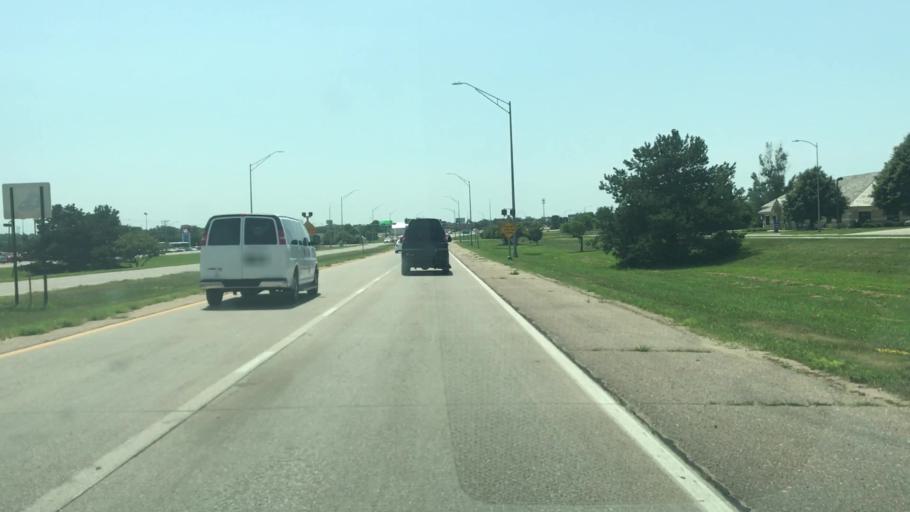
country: US
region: Nebraska
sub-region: Adams County
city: Hastings
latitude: 40.6161
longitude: -98.3832
